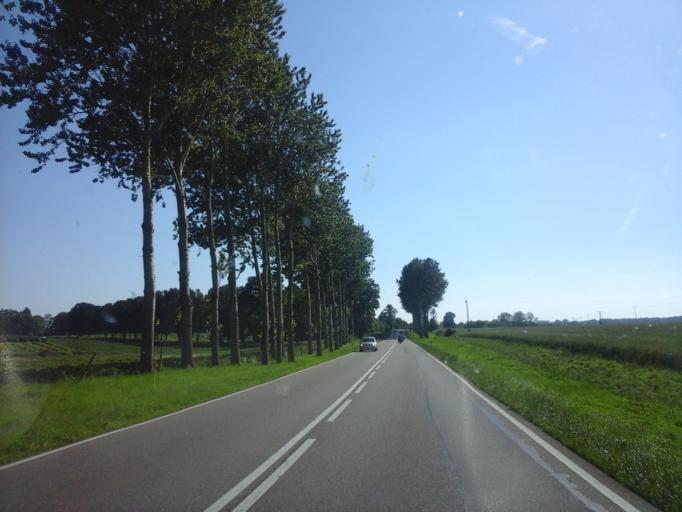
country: PL
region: West Pomeranian Voivodeship
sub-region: Powiat gryficki
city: Brojce
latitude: 53.8841
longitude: 15.4006
